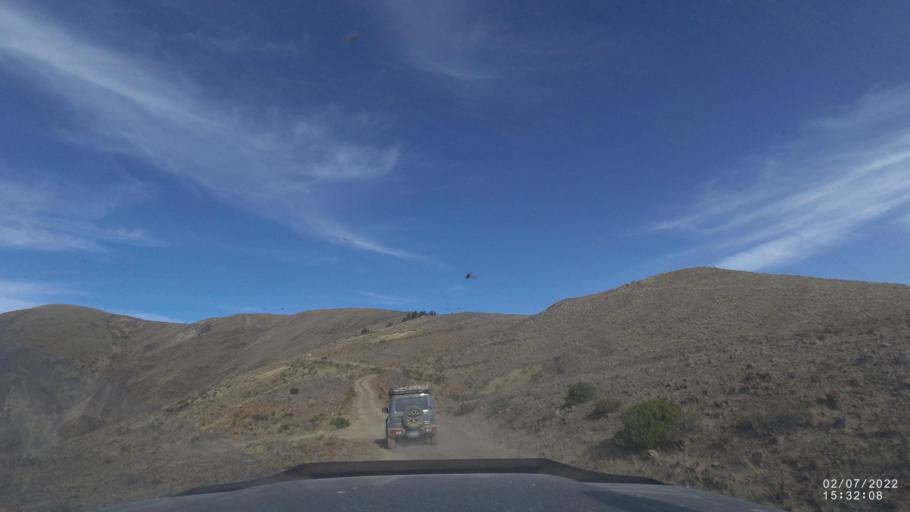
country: BO
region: Cochabamba
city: Irpa Irpa
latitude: -17.8838
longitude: -66.4142
